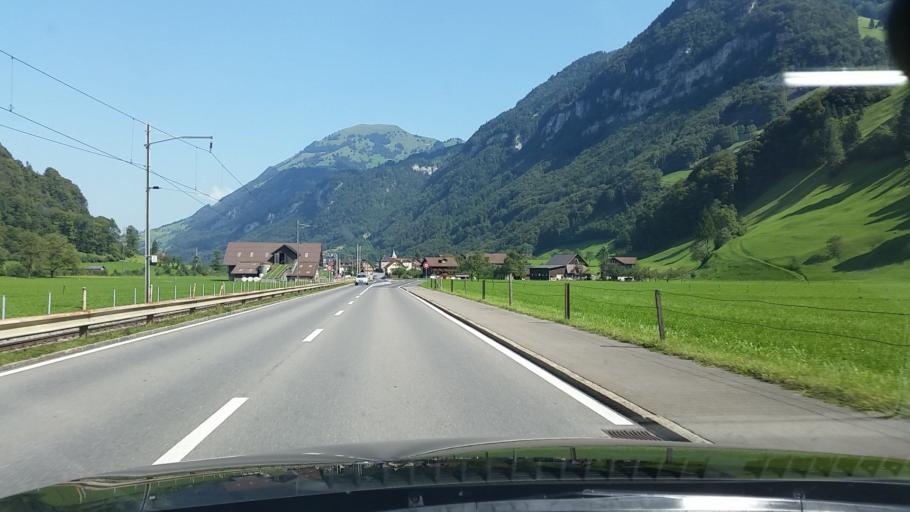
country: CH
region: Nidwalden
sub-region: Nidwalden
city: Wolfenschiessen
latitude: 46.8932
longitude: 8.3876
